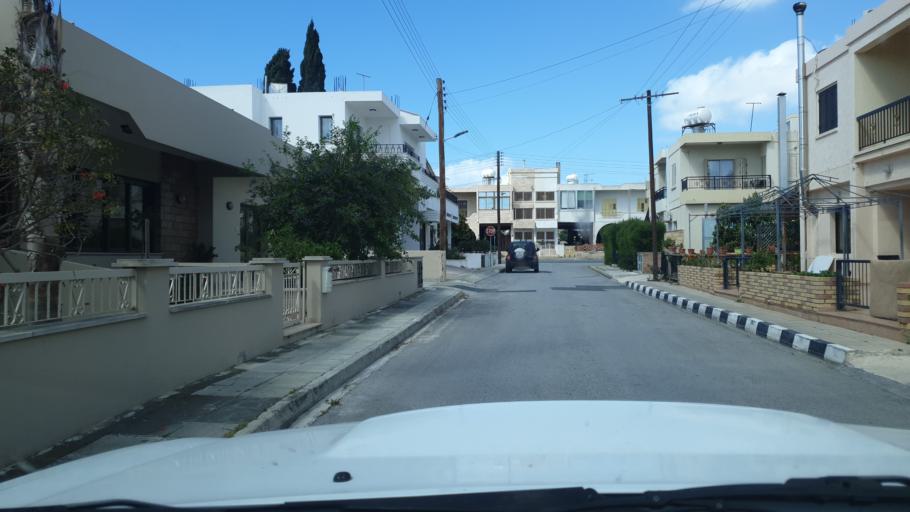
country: CY
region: Pafos
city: Paphos
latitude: 34.7620
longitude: 32.4481
